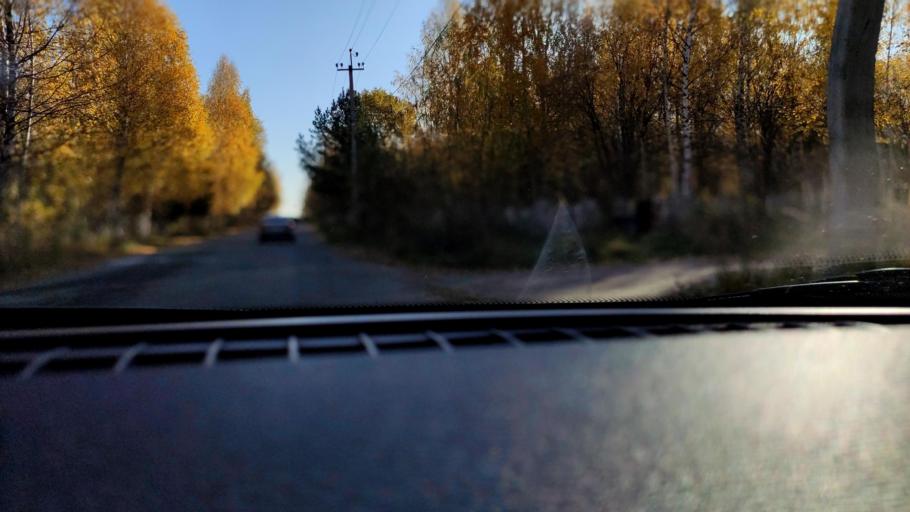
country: RU
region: Perm
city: Kondratovo
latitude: 58.0635
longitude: 56.1373
